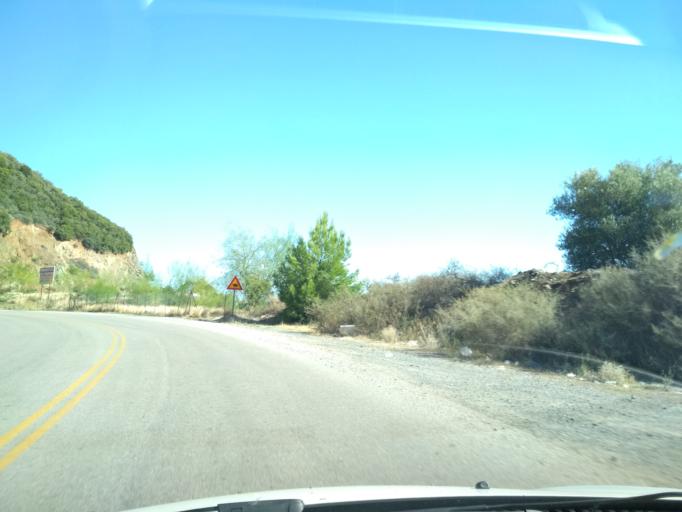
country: GR
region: Central Greece
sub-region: Nomos Evvoias
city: Oreoi
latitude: 38.8489
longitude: 23.0658
